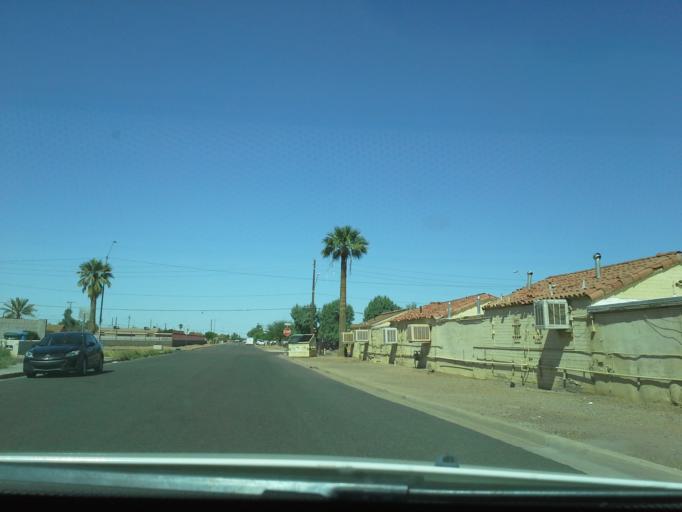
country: US
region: Arizona
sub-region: Maricopa County
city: Phoenix
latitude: 33.4386
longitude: -112.0948
